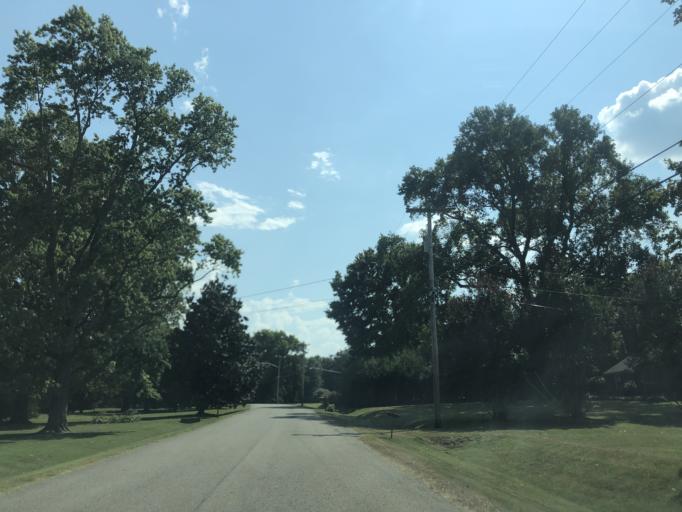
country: US
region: Tennessee
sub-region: Davidson County
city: Oak Hill
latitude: 36.0940
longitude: -86.7662
